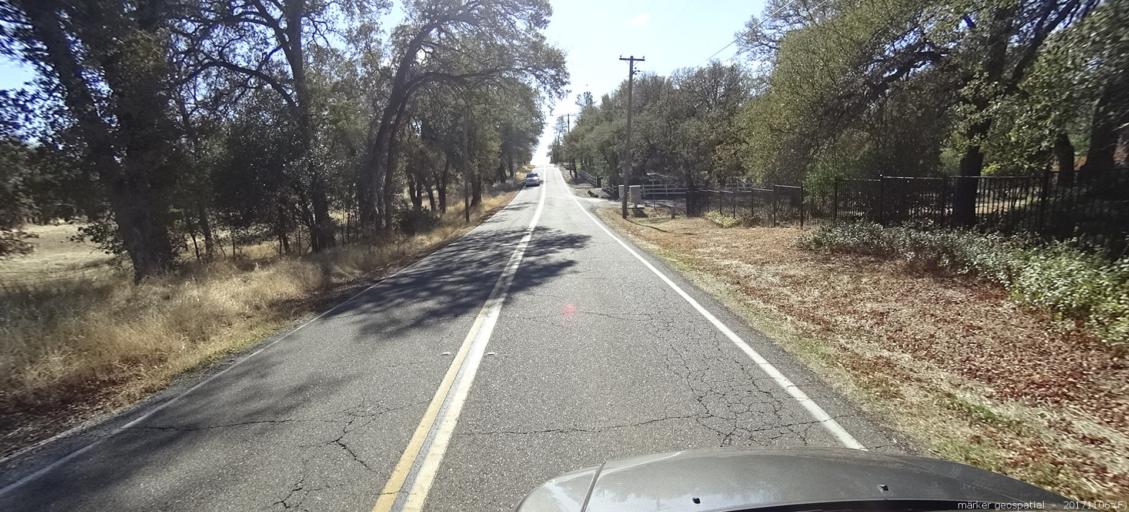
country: US
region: California
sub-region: Shasta County
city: Palo Cedro
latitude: 40.5695
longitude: -122.2199
